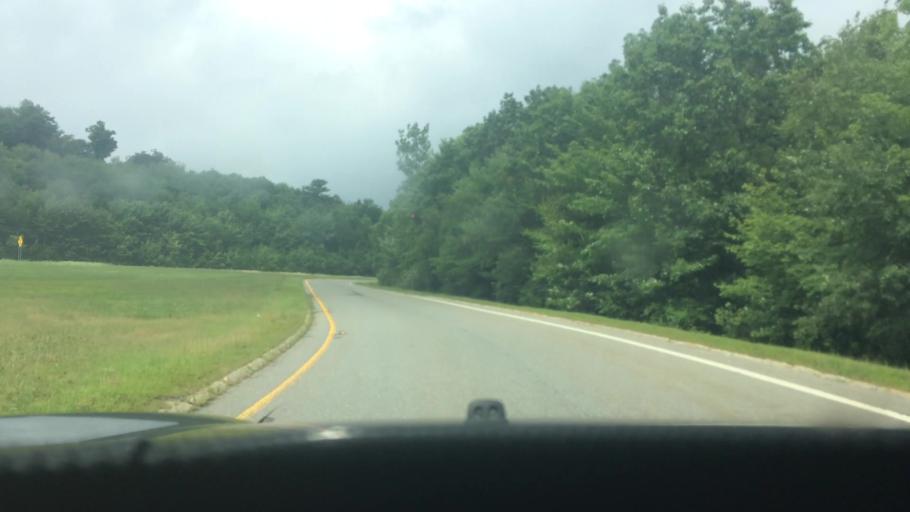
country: US
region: Massachusetts
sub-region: Worcester County
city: Templeton
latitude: 42.5601
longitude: -72.0476
